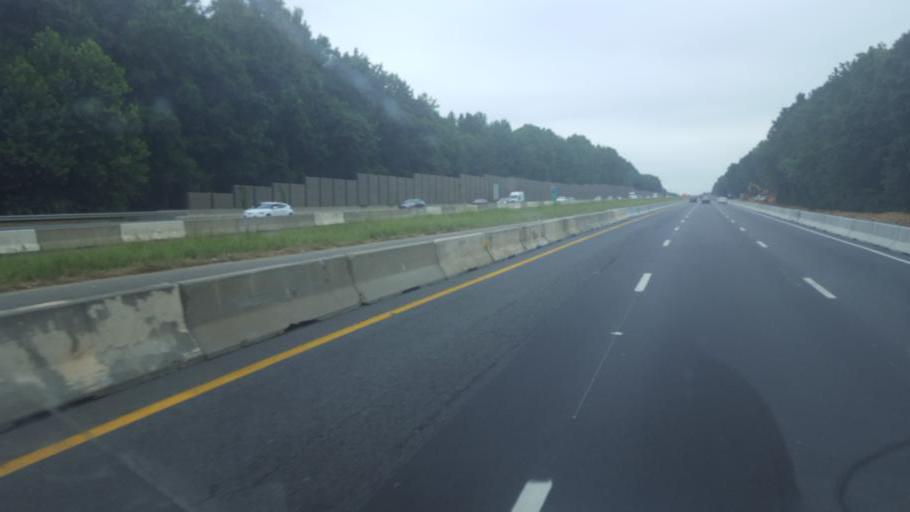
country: US
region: North Carolina
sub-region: Mecklenburg County
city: Charlotte
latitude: 35.2954
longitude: -80.8508
